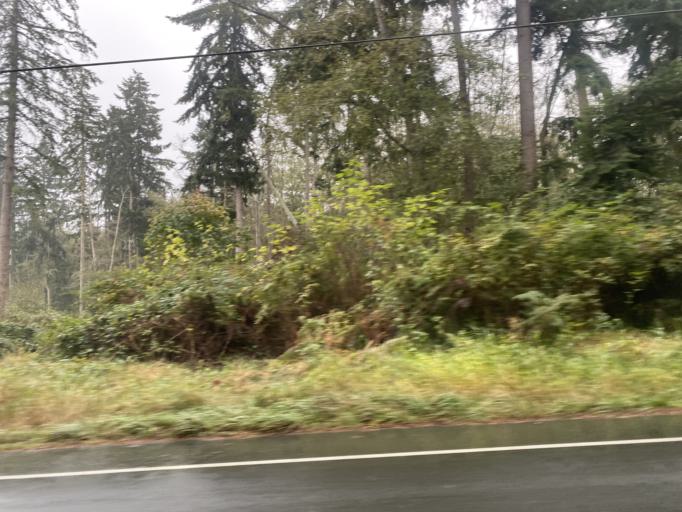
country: US
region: Washington
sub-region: Island County
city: Freeland
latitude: 48.0211
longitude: -122.5168
